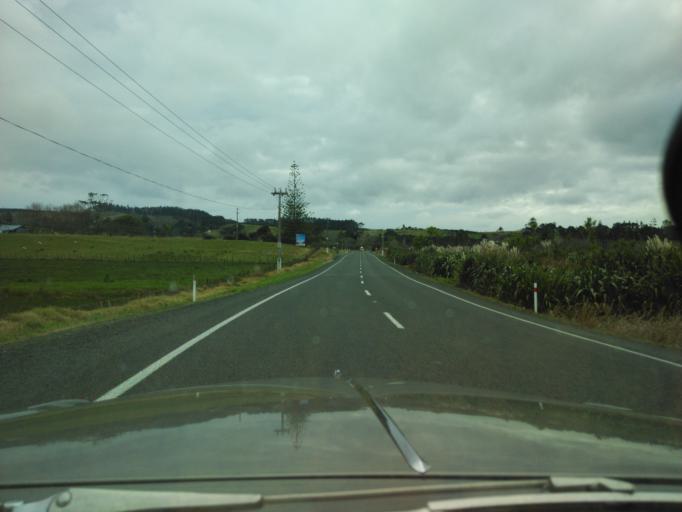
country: NZ
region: Auckland
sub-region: Auckland
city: Muriwai Beach
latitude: -36.7517
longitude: 174.4432
